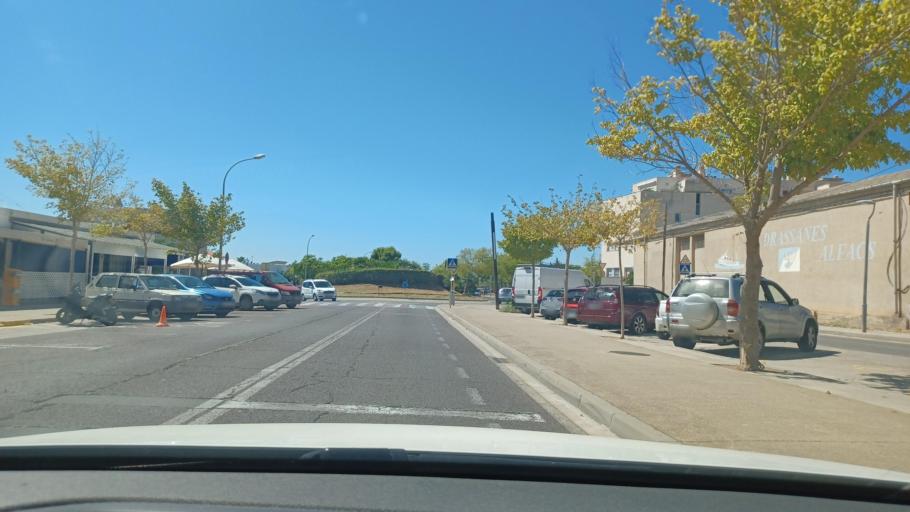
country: ES
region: Catalonia
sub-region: Provincia de Tarragona
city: Sant Carles de la Rapita
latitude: 40.6122
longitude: 0.5857
